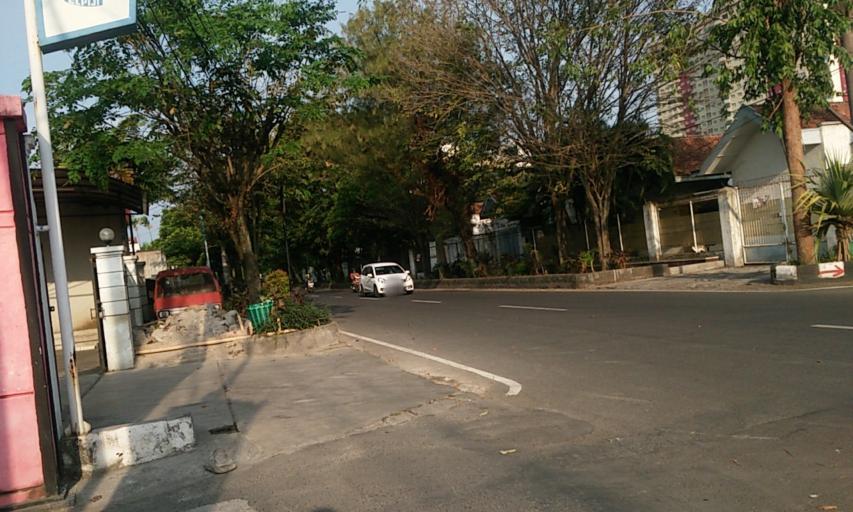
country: ID
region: Central Java
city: Surakarta
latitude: -7.5608
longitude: 110.8084
